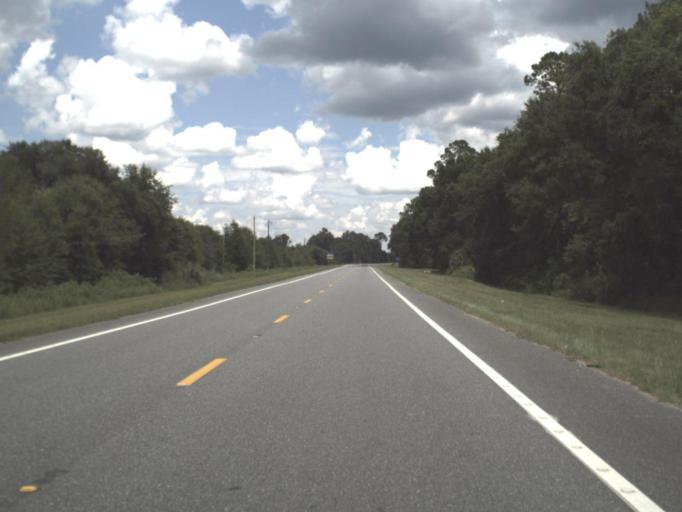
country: US
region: Florida
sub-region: Taylor County
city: Perry
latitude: 30.0865
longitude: -83.4978
